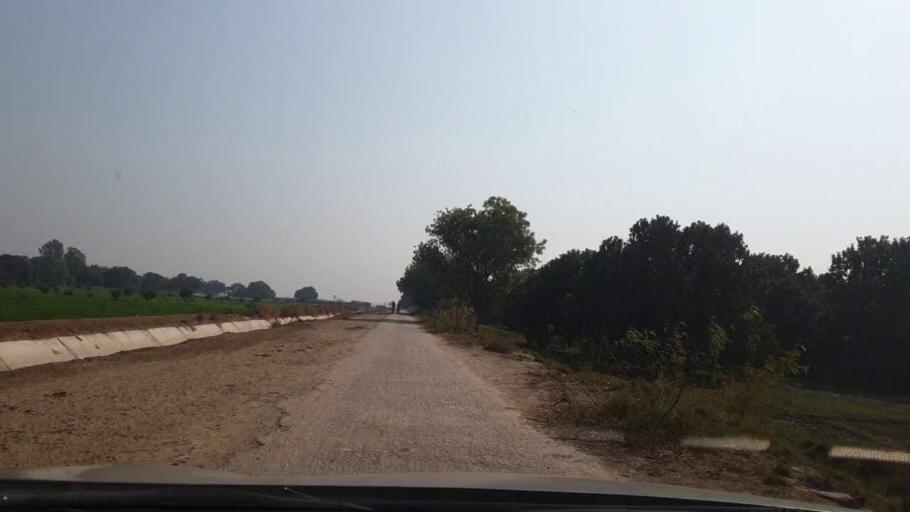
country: PK
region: Sindh
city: Tando Allahyar
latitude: 25.5197
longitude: 68.7832
